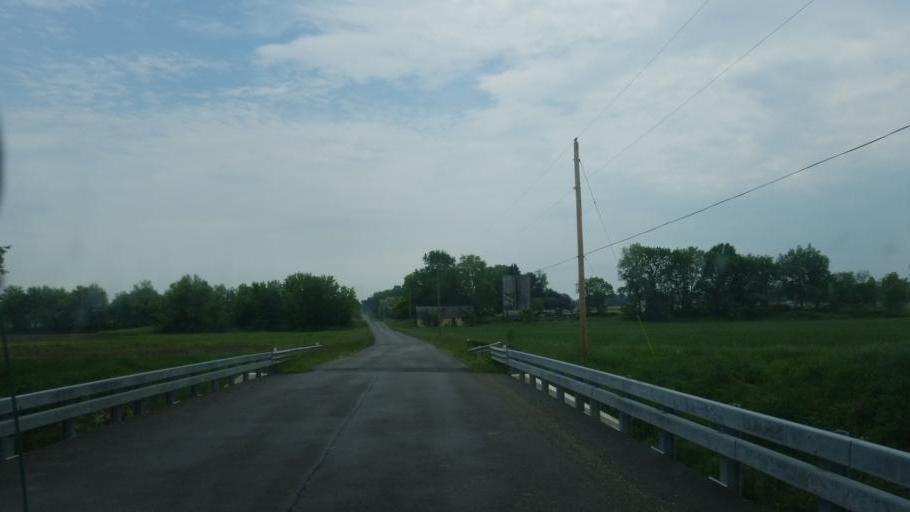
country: US
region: Ohio
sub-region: Wayne County
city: Orrville
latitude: 40.8046
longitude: -81.7552
